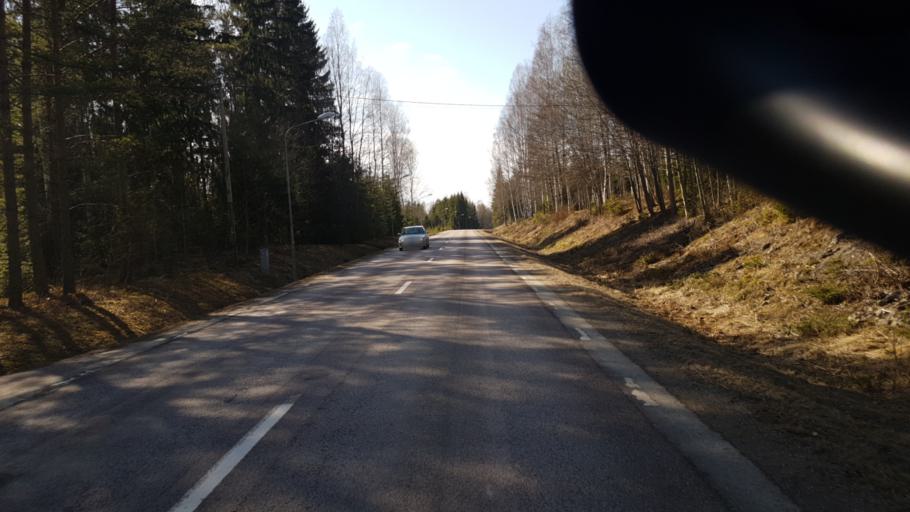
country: SE
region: Vaermland
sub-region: Arvika Kommun
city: Arvika
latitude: 59.6466
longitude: 12.7643
